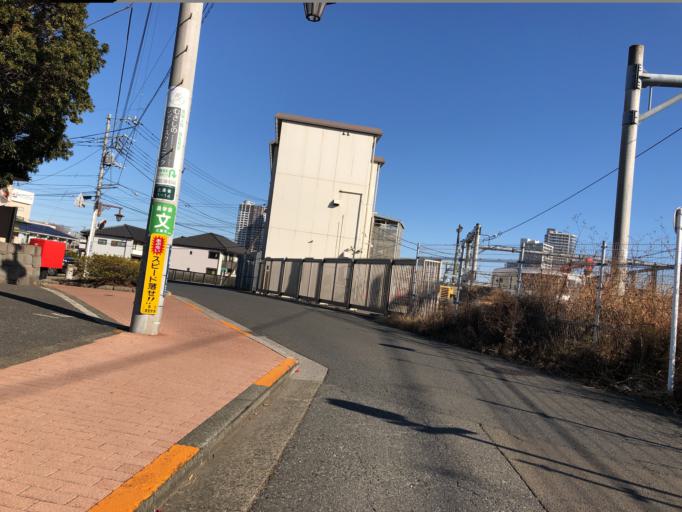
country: JP
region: Tokyo
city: Kamirenjaku
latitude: 35.7025
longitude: 139.5534
